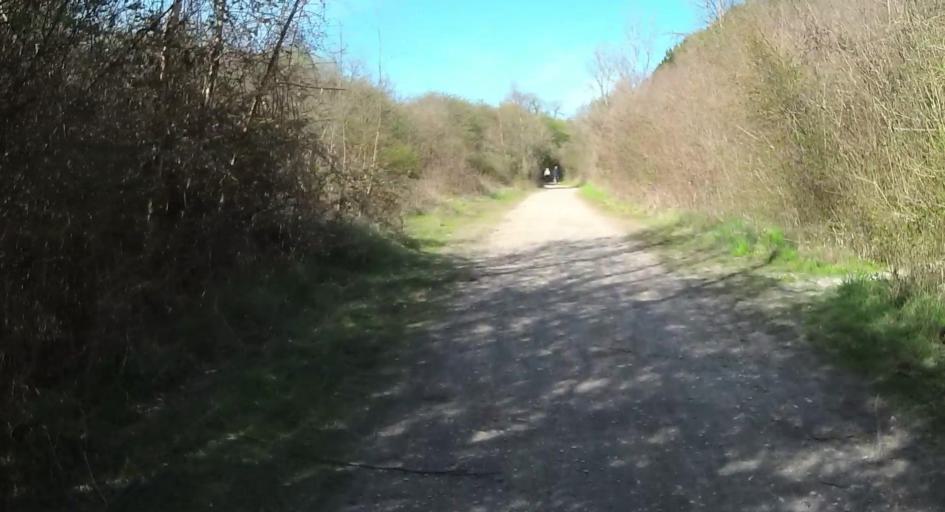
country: GB
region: England
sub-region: Hampshire
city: Romsey
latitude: 51.0862
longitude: -1.5016
